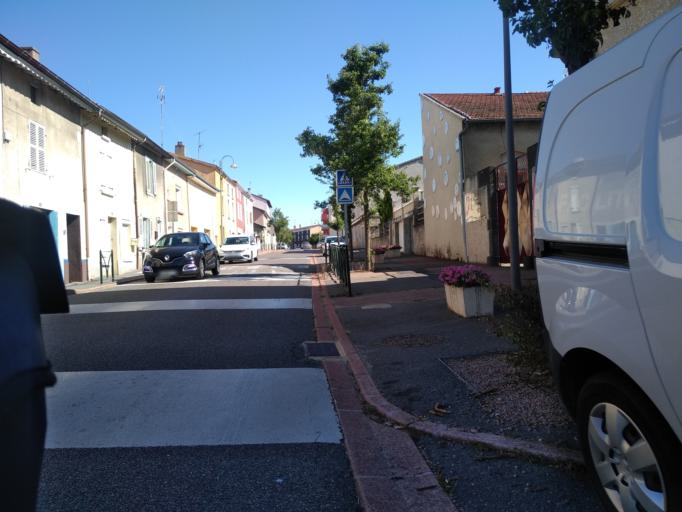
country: FR
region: Rhone-Alpes
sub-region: Departement de la Loire
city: Neulise
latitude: 45.8988
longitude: 4.1817
